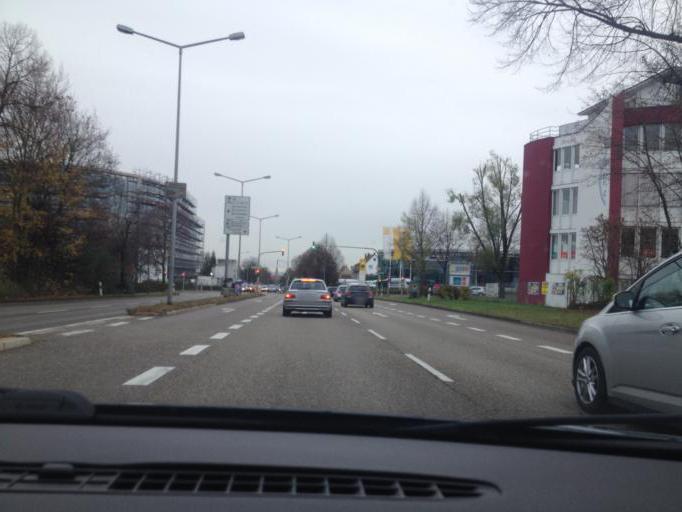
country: DE
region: Baden-Wuerttemberg
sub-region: Regierungsbezirk Stuttgart
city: Ludwigsburg
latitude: 48.8901
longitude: 9.1620
